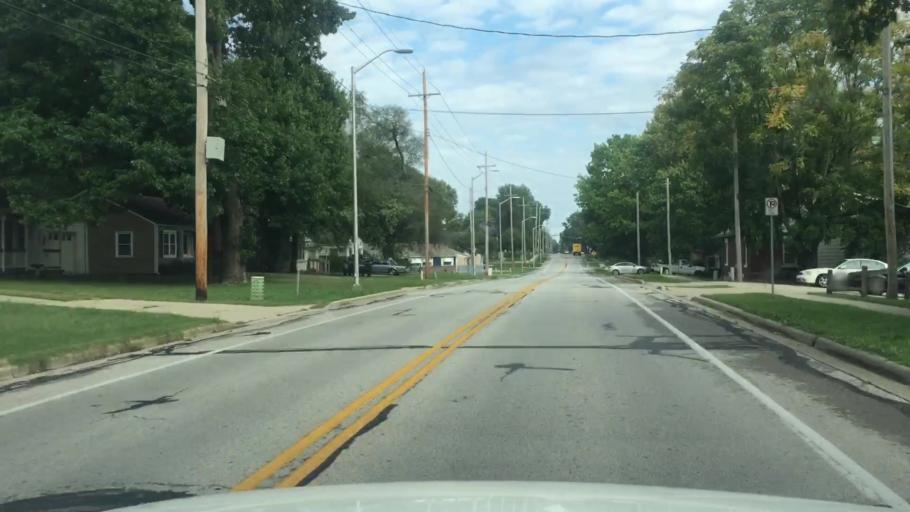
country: US
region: Kansas
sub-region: Johnson County
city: Shawnee
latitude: 39.0292
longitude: -94.7277
